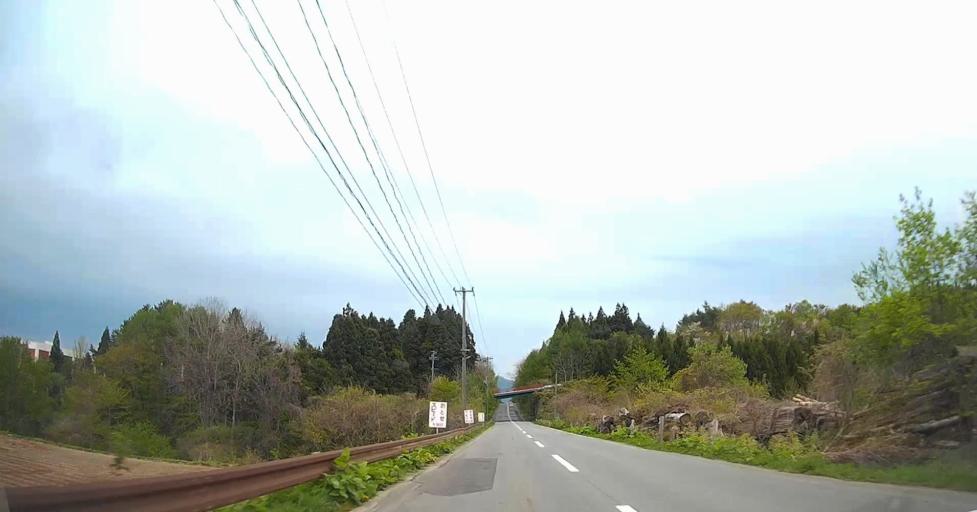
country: JP
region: Aomori
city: Shimokizukuri
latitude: 41.1789
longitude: 140.4695
